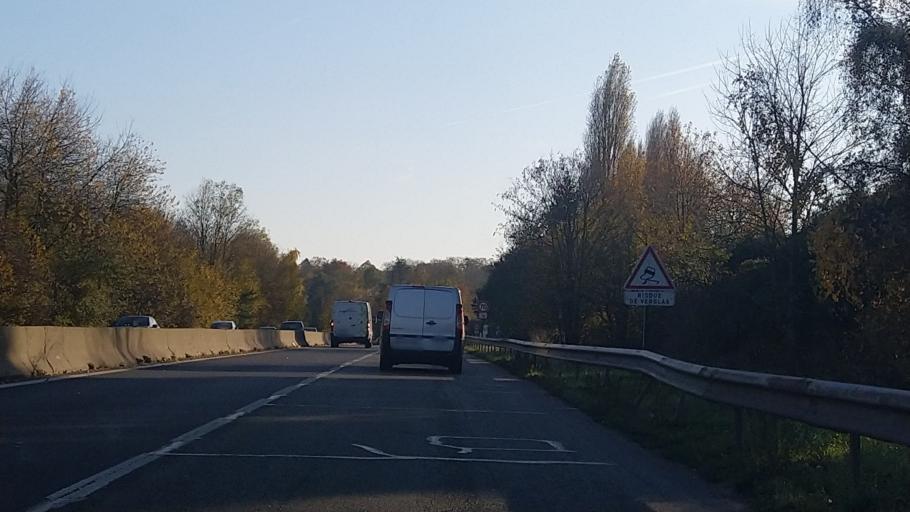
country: FR
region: Ile-de-France
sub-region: Departement du Val-d'Oise
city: Domont
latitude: 49.0306
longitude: 2.3467
